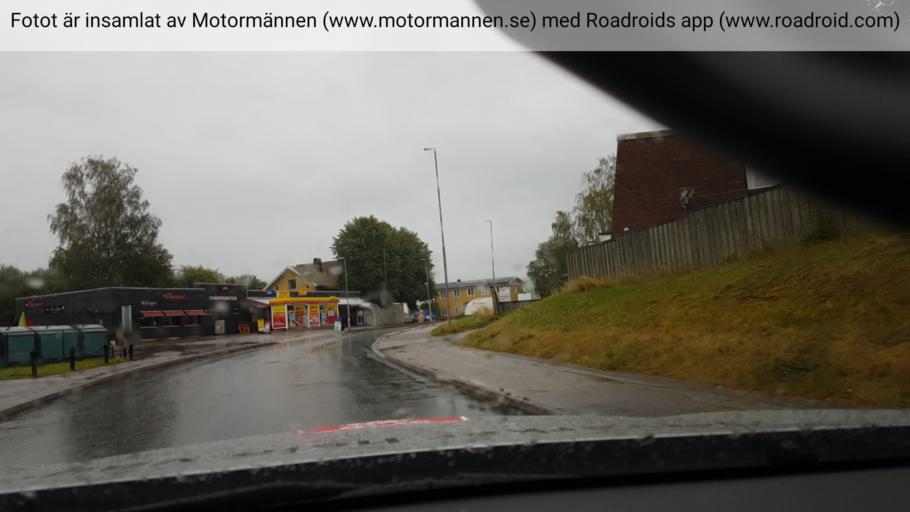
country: SE
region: Vaestra Goetaland
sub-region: Harryda Kommun
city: Hindas
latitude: 57.7037
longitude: 12.4396
